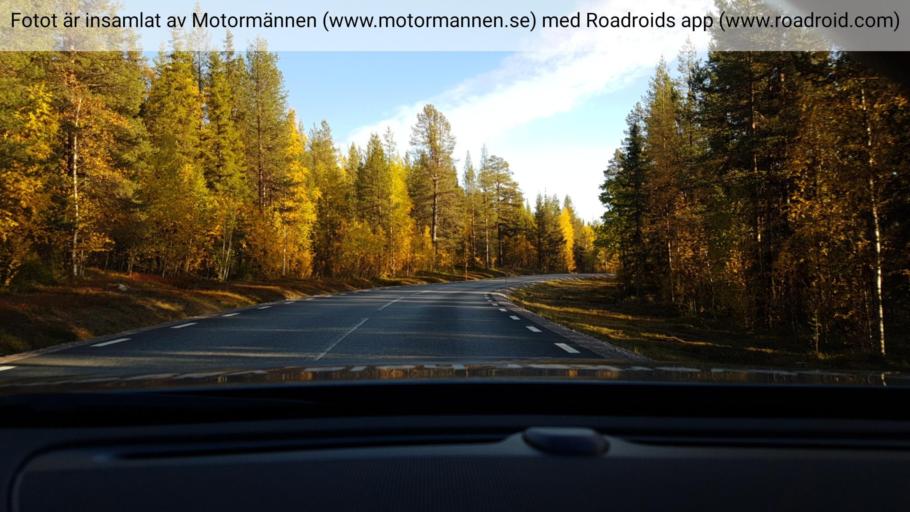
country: SE
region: Norrbotten
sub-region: Jokkmokks Kommun
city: Jokkmokk
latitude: 66.9367
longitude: 19.8164
